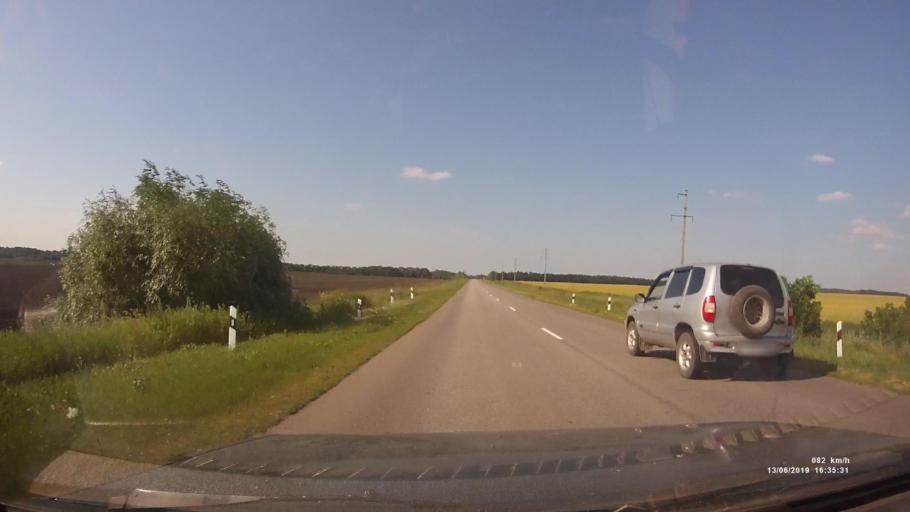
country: RU
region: Rostov
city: Kazanskaya
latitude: 49.8832
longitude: 41.2987
